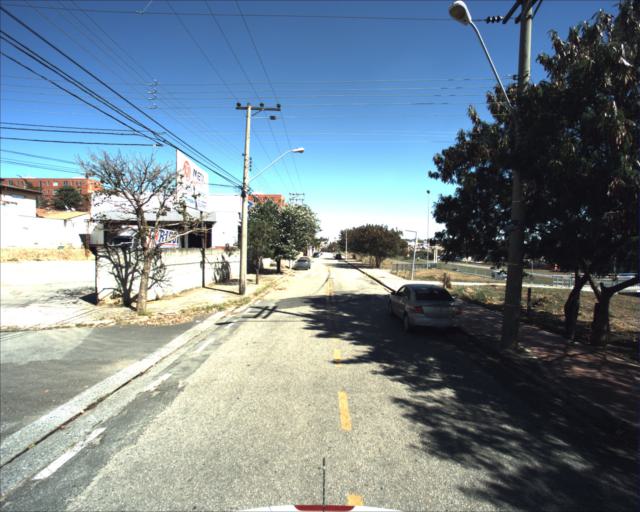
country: BR
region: Sao Paulo
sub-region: Sorocaba
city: Sorocaba
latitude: -23.4762
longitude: -47.4347
